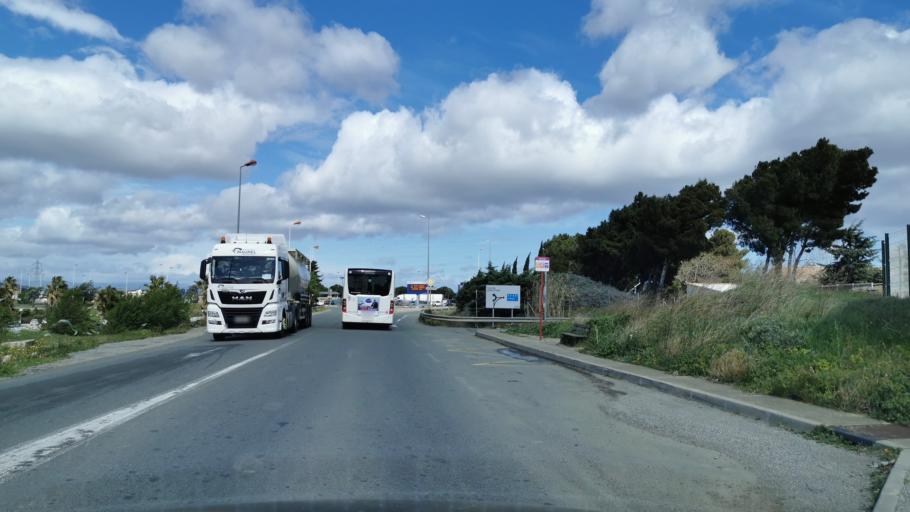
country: FR
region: Languedoc-Roussillon
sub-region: Departement de l'Aude
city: Narbonne
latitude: 43.1633
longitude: 2.9887
